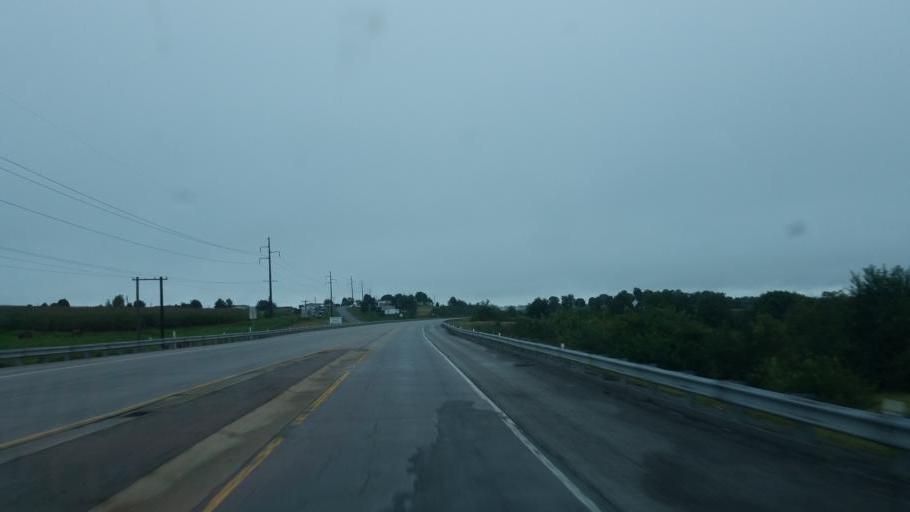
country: US
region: Kentucky
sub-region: Fleming County
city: Flemingsburg
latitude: 38.4110
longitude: -83.7357
